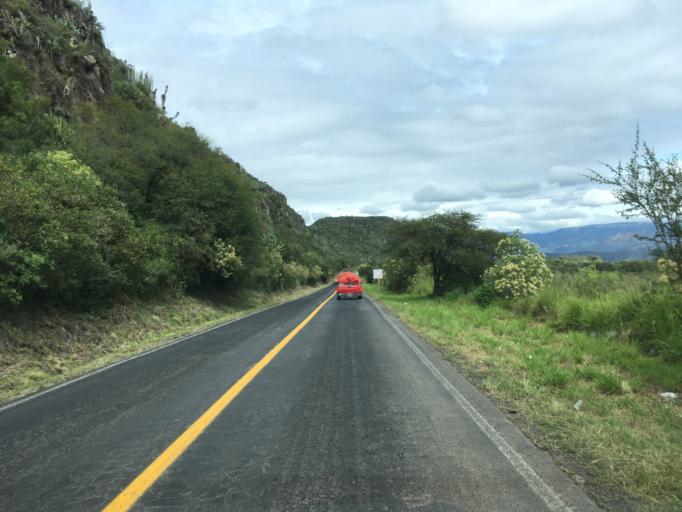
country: MX
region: Hidalgo
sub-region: Atotonilco el Grande
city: Santa Maria Amajac
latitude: 20.4187
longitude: -98.6872
